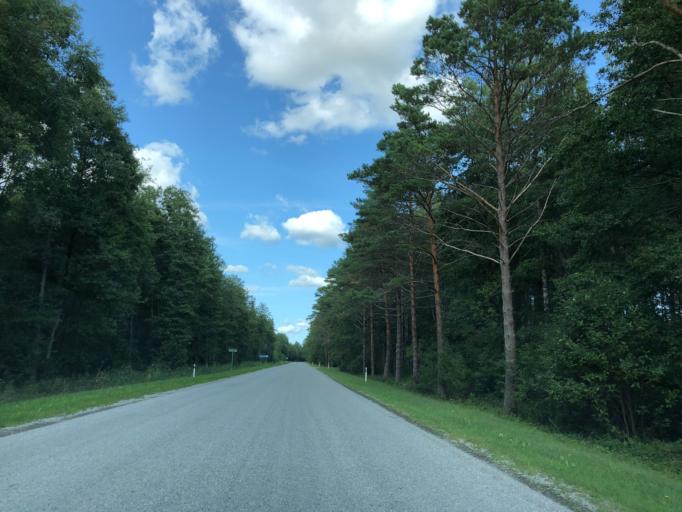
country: EE
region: Hiiumaa
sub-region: Kaerdla linn
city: Kardla
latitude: 58.8152
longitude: 22.7361
